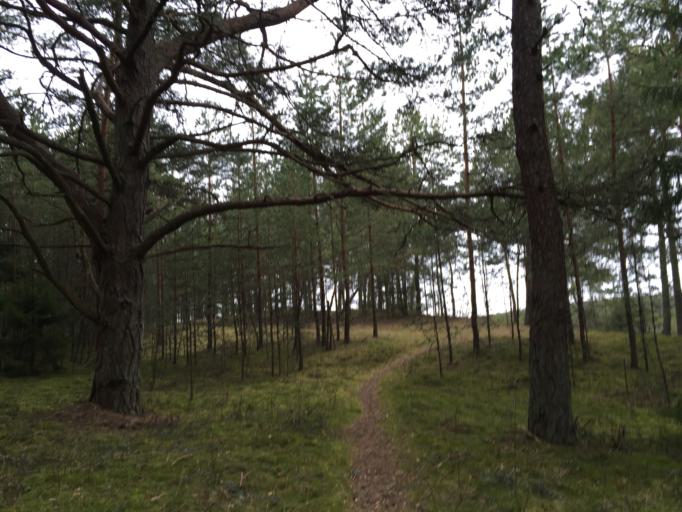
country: LT
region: Klaipedos apskritis
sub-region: Klaipeda
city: Klaipeda
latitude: 55.5589
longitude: 21.1219
